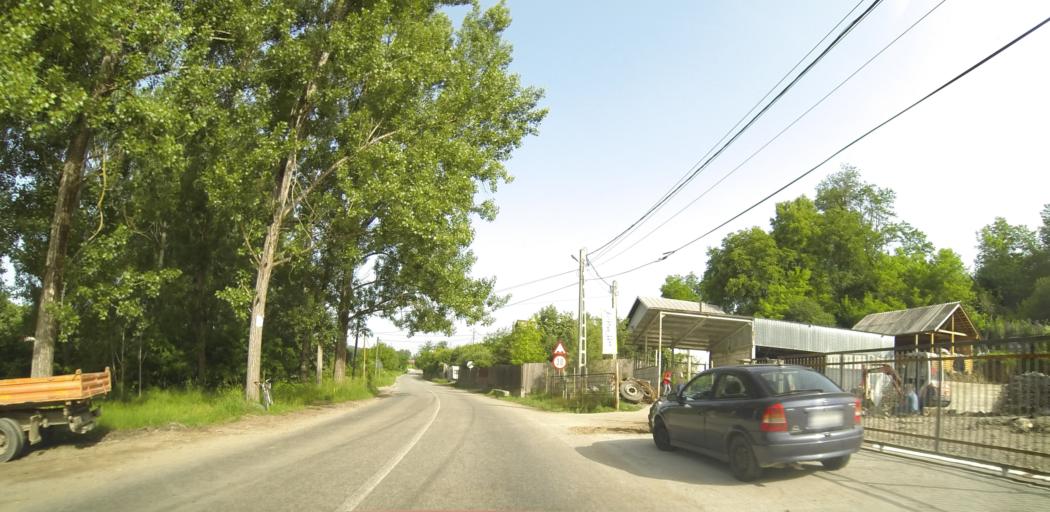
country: RO
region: Valcea
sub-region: Comuna Pausesti-Maglasi
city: Pausesti-Maglasi
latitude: 45.1315
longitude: 24.2601
